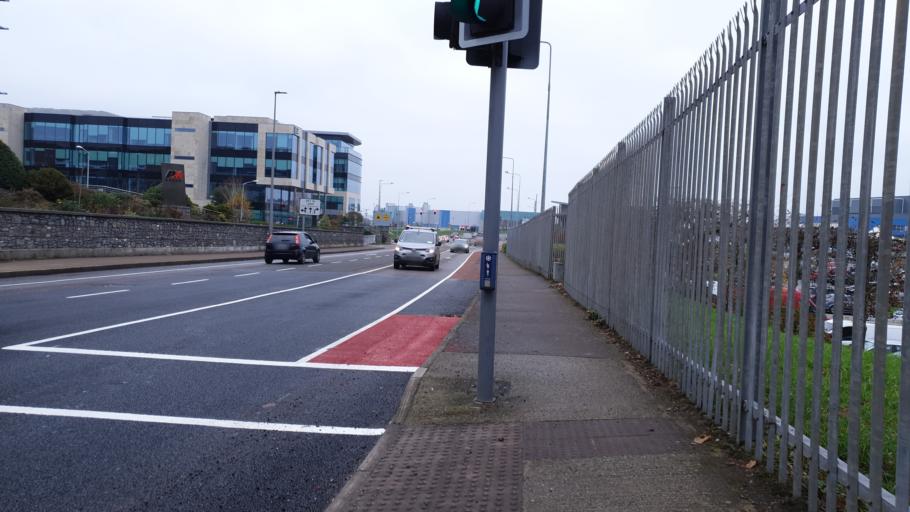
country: IE
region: Munster
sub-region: County Cork
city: Passage West
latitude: 51.8854
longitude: -8.4041
